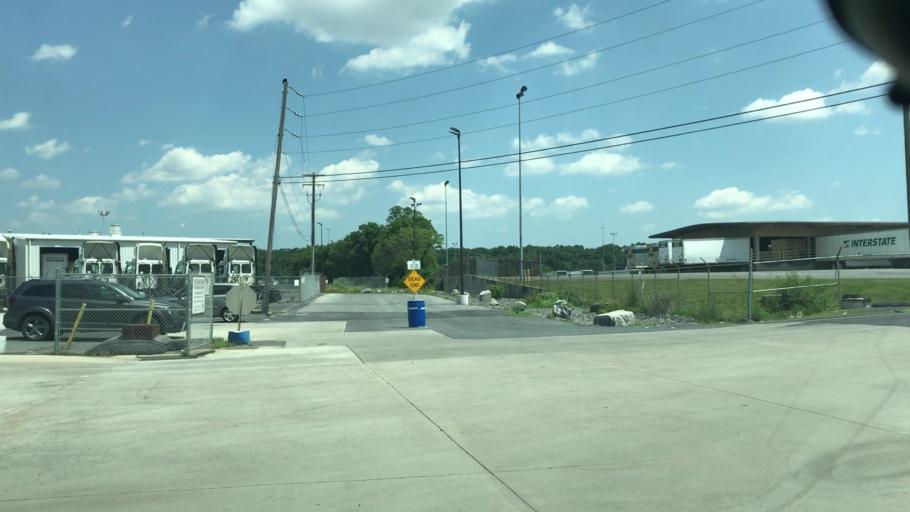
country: US
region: Pennsylvania
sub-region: Cumberland County
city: Schlusser
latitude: 40.2393
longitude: -77.1163
